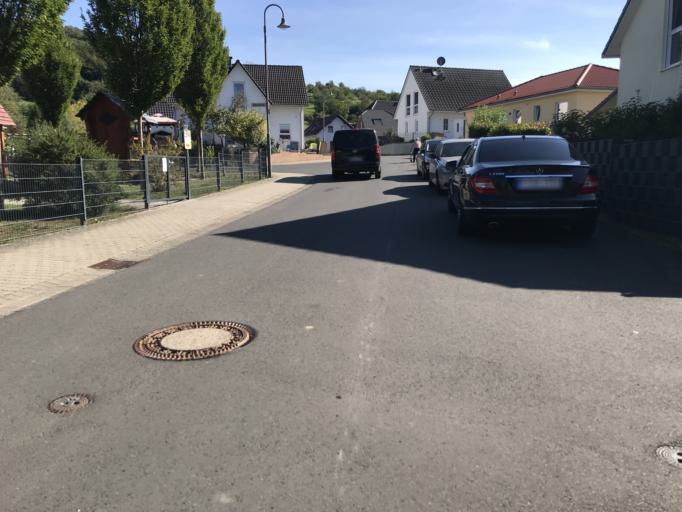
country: DE
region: Hesse
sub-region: Regierungsbezirk Darmstadt
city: Glauburg
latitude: 50.3129
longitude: 9.0004
